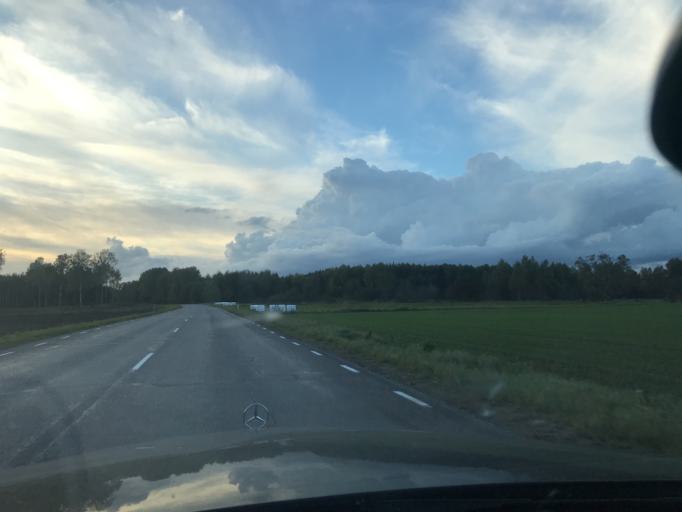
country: EE
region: Vorumaa
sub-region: Antsla vald
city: Vana-Antsla
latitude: 57.9036
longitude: 26.4633
